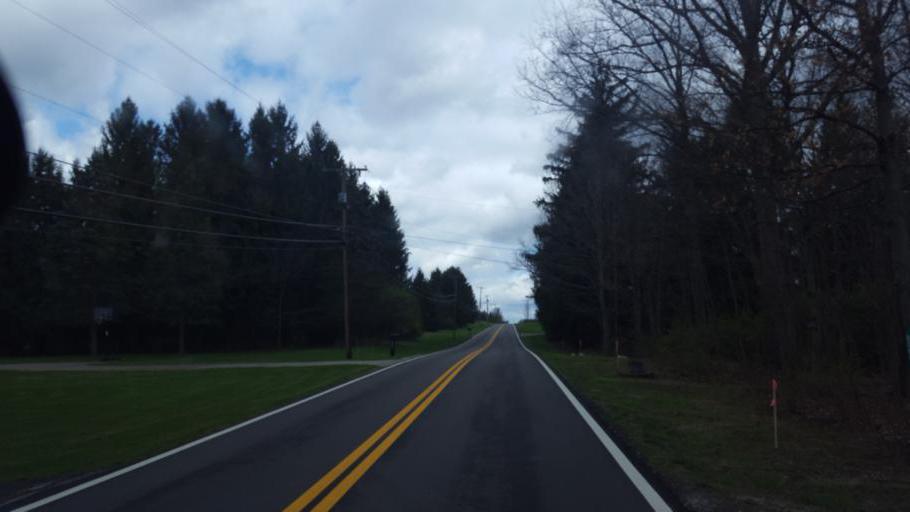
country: US
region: Ohio
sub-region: Franklin County
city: New Albany
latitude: 40.1222
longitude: -82.8588
